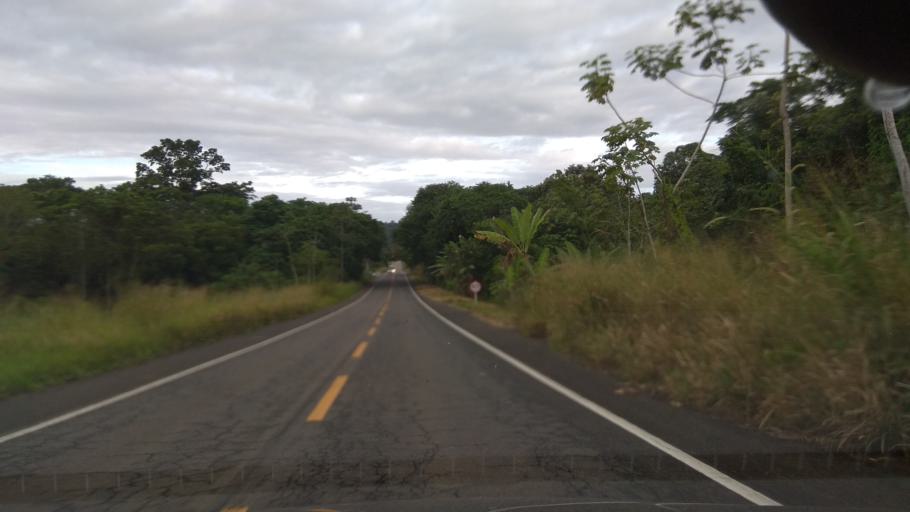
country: BR
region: Bahia
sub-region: Ubaitaba
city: Ubaitaba
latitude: -14.2634
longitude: -39.3318
